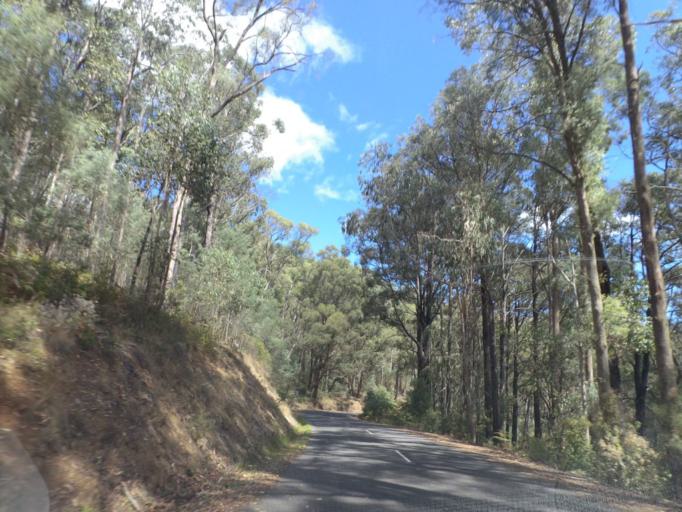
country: AU
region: Victoria
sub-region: Murrindindi
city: Alexandra
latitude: -37.3350
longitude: 145.9531
